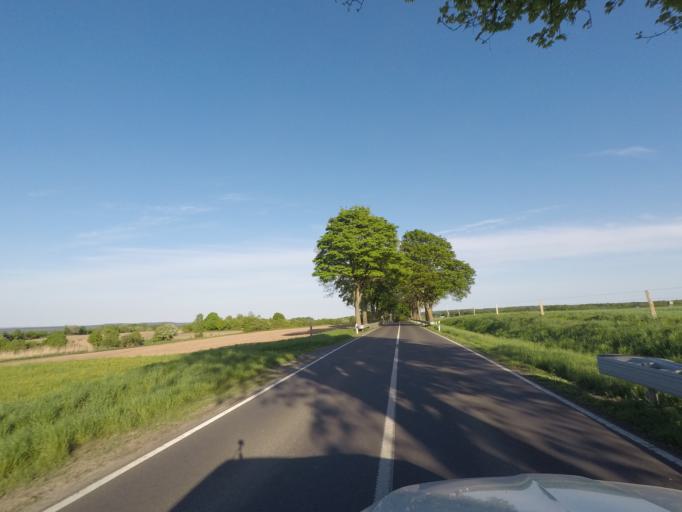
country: DE
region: Brandenburg
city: Hohenfinow
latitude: 52.8080
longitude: 13.9307
